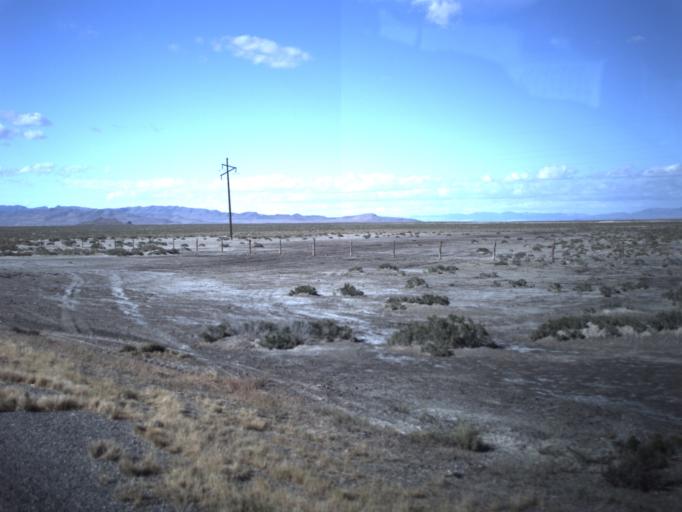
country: US
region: Utah
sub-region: Millard County
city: Delta
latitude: 39.1777
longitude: -112.7020
